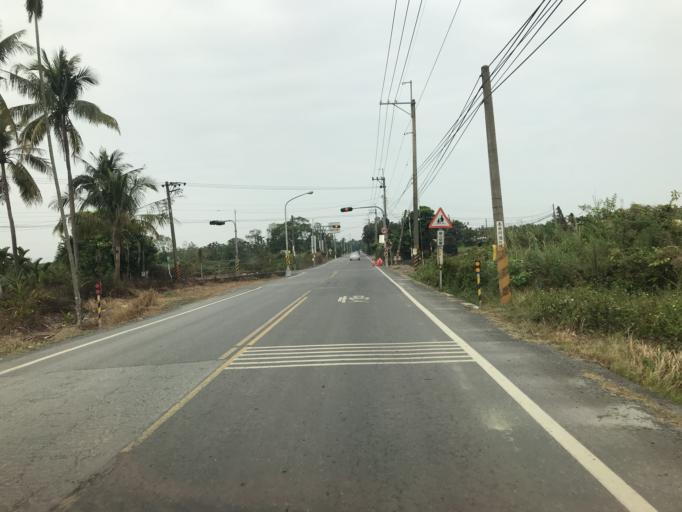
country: TW
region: Taiwan
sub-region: Pingtung
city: Pingtung
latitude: 22.4714
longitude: 120.6079
